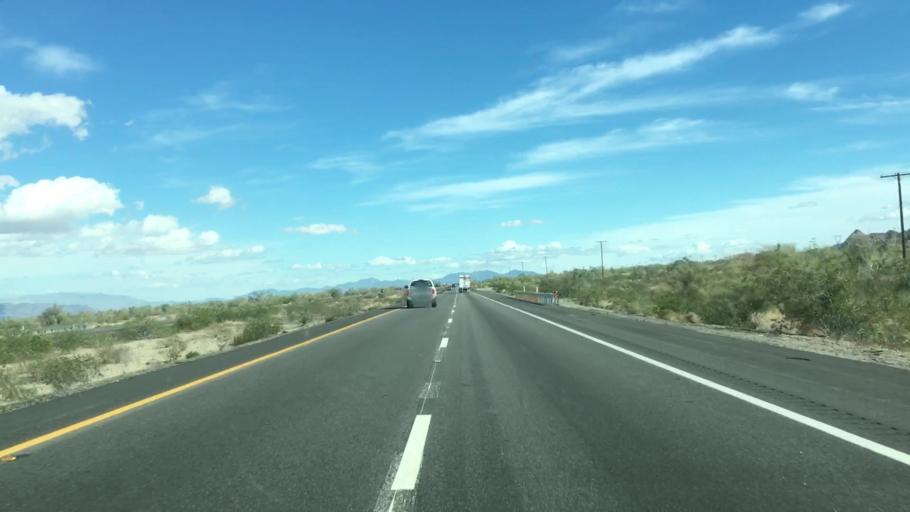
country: US
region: California
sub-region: Imperial County
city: Niland
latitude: 33.6926
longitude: -115.4960
